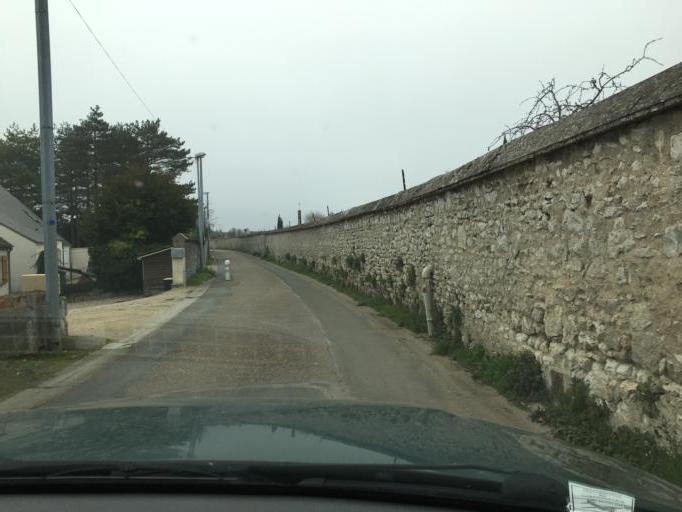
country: FR
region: Centre
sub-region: Departement du Loiret
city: Beaugency
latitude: 47.7826
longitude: 1.6366
